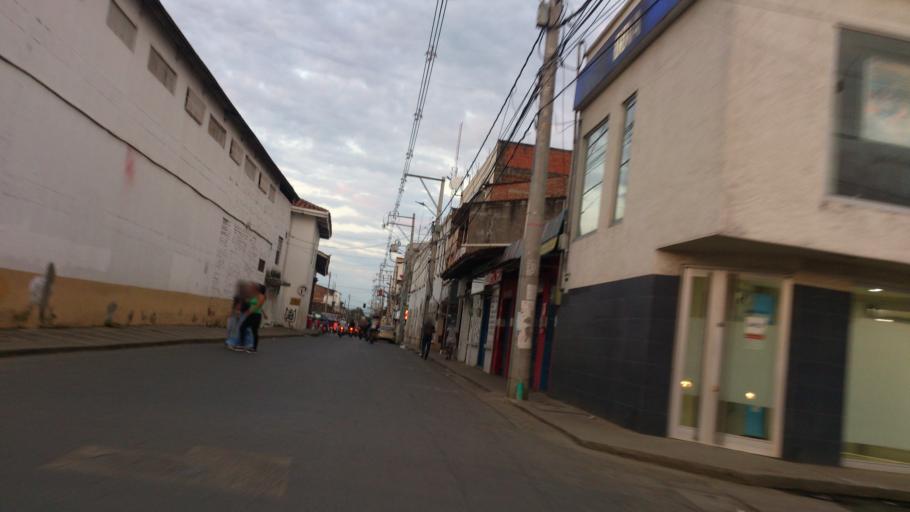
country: CO
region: Valle del Cauca
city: Jamundi
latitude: 3.2606
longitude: -76.5415
